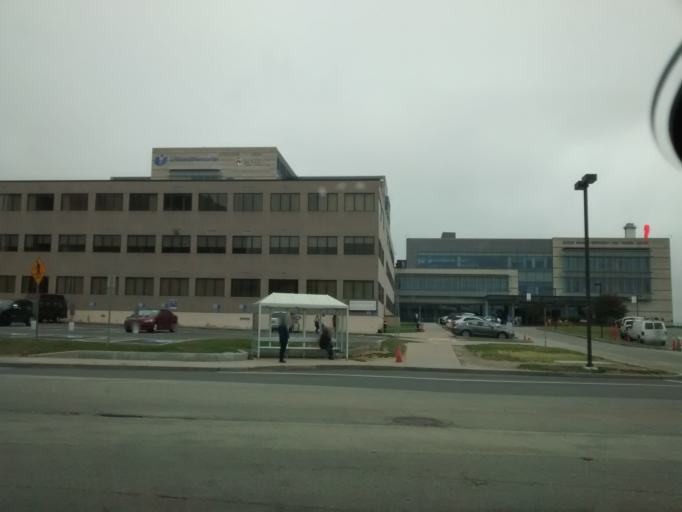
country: US
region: Massachusetts
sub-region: Worcester County
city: Hamilton
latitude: 42.2755
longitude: -71.7616
